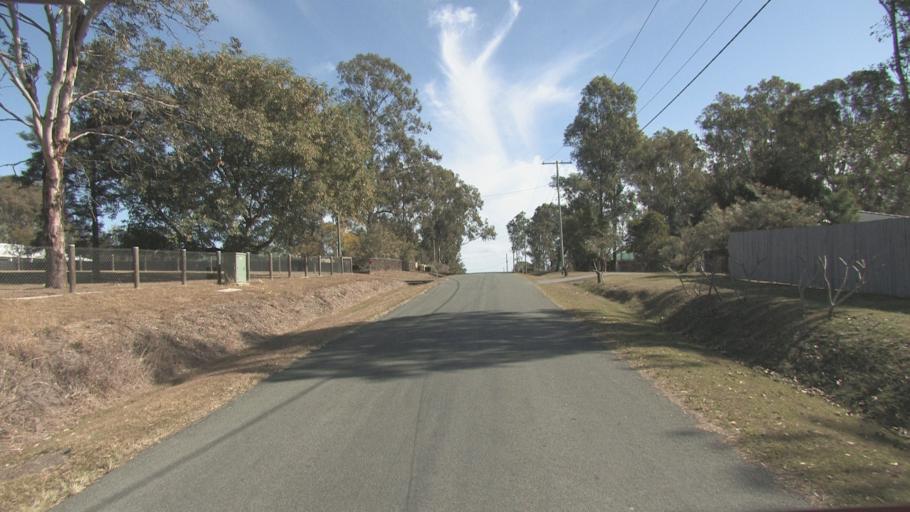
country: AU
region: Queensland
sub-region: Logan
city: Cedar Vale
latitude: -27.8690
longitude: 152.9754
